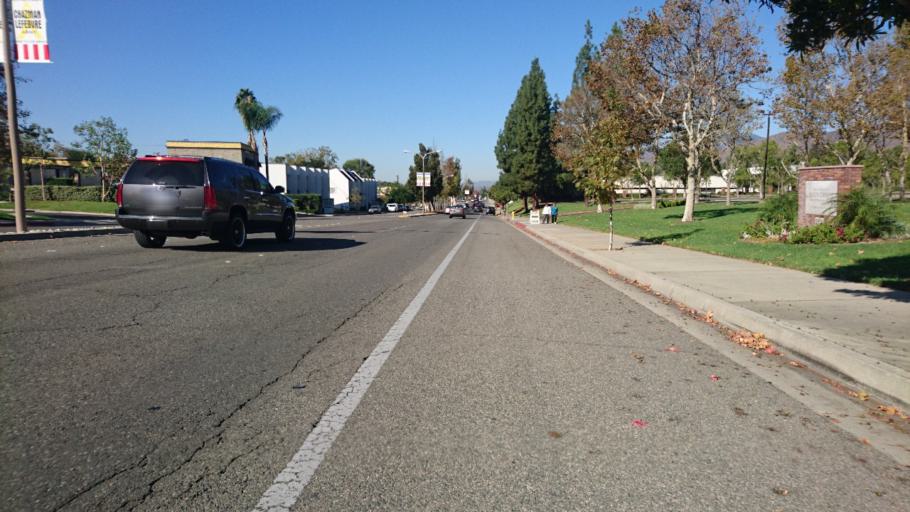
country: US
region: California
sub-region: Los Angeles County
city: San Dimas
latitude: 34.1278
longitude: -117.8239
